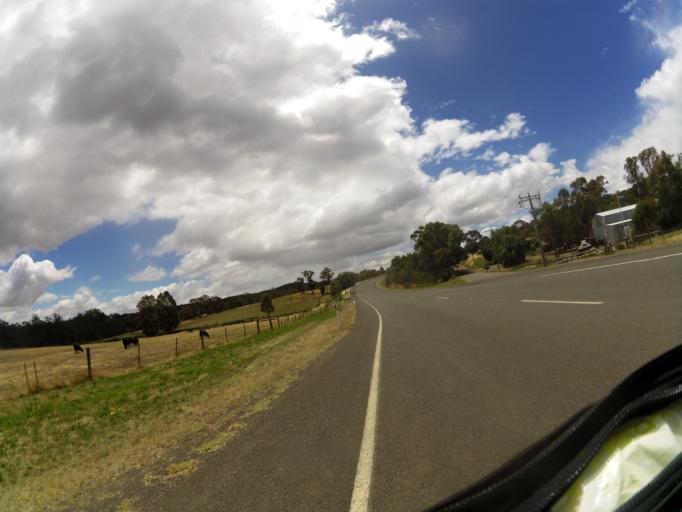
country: AU
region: Victoria
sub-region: Mount Alexander
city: Castlemaine
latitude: -37.0124
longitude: 144.2511
